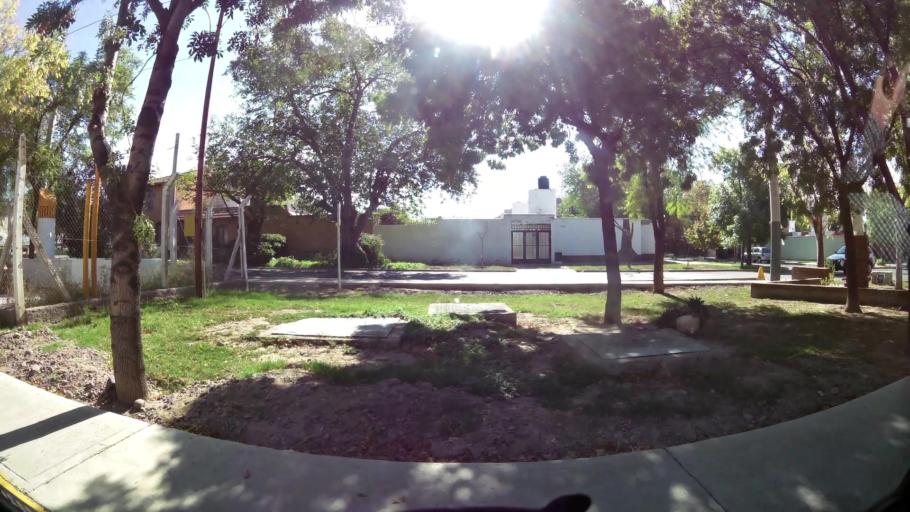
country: AR
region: Mendoza
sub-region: Departamento de Godoy Cruz
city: Godoy Cruz
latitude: -32.9252
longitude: -68.8325
